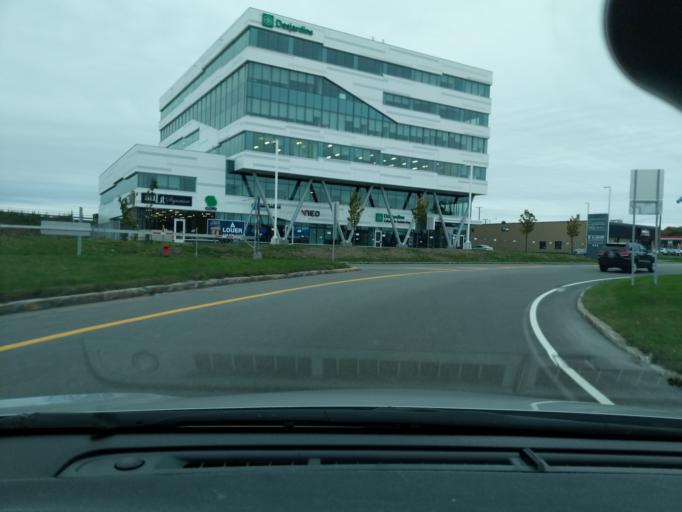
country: CA
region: Quebec
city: L'Ancienne-Lorette
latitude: 46.7647
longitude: -71.3118
